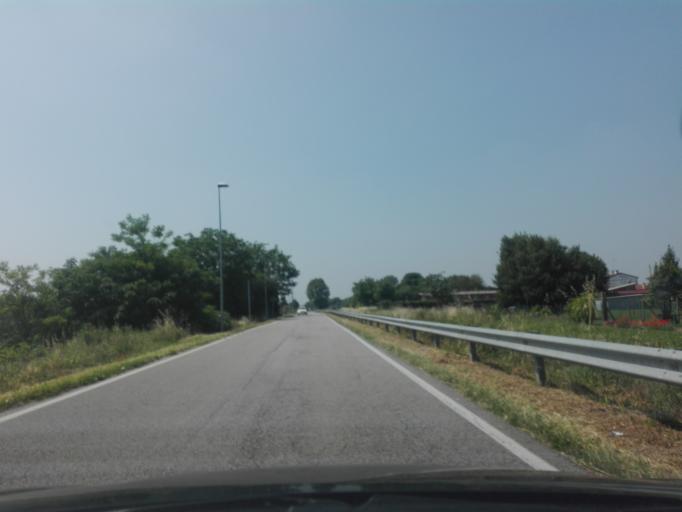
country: IT
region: Veneto
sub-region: Provincia di Rovigo
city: Ceregnano
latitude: 45.0663
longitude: 11.8726
